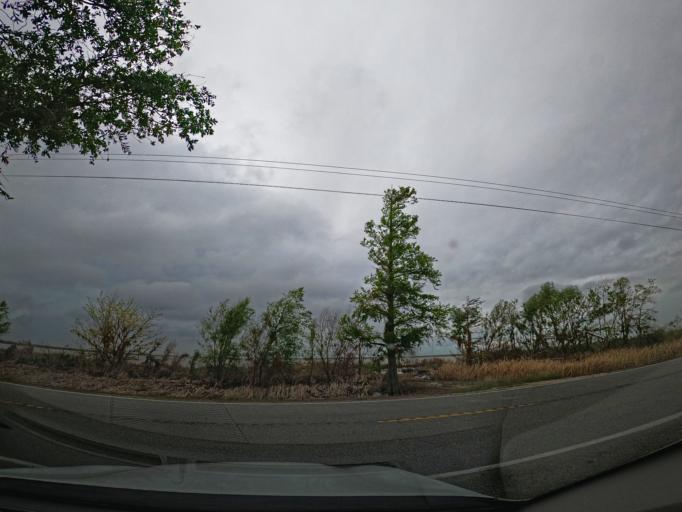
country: US
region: Louisiana
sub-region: Cameron Parish
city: Cameron
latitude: 29.7545
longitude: -92.9184
